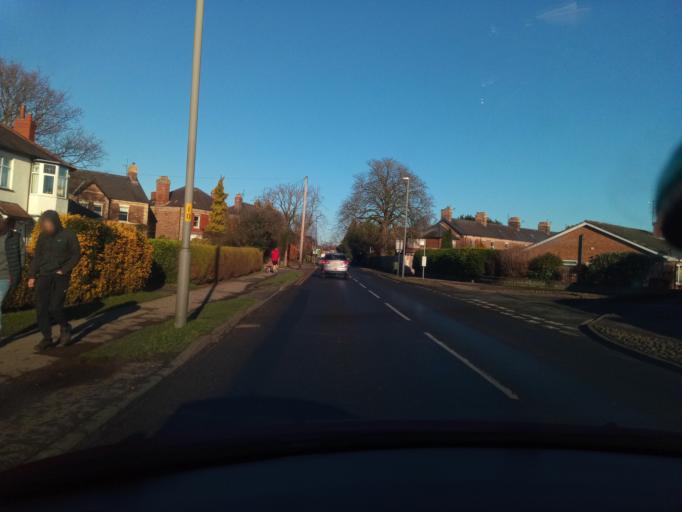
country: GB
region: England
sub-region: North Yorkshire
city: Thirsk
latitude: 54.2278
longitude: -1.3470
